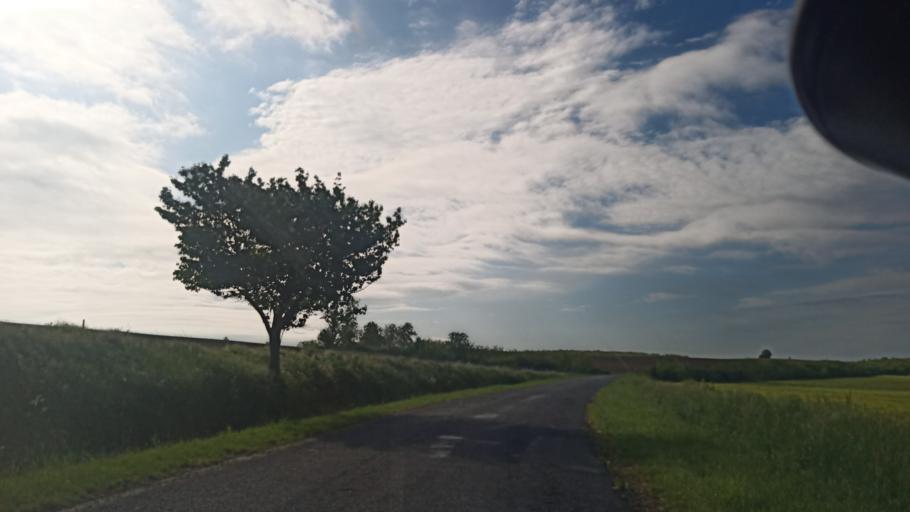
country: HU
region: Zala
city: Pacsa
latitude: 46.7047
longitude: 17.0522
